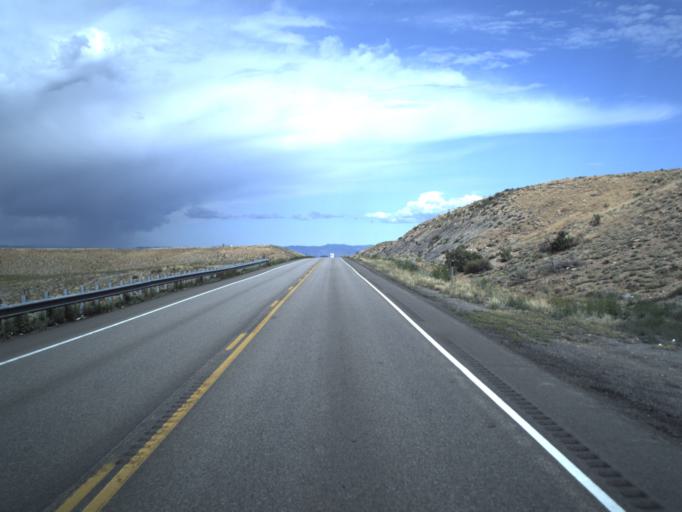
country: US
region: Utah
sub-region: Carbon County
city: East Carbon City
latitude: 39.5154
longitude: -110.5493
